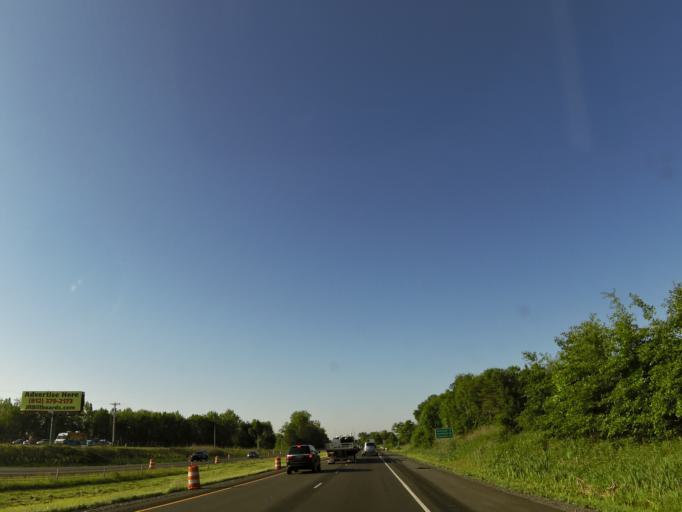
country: US
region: Indiana
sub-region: Jackson County
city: Seymour
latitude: 38.9455
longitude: -85.8435
